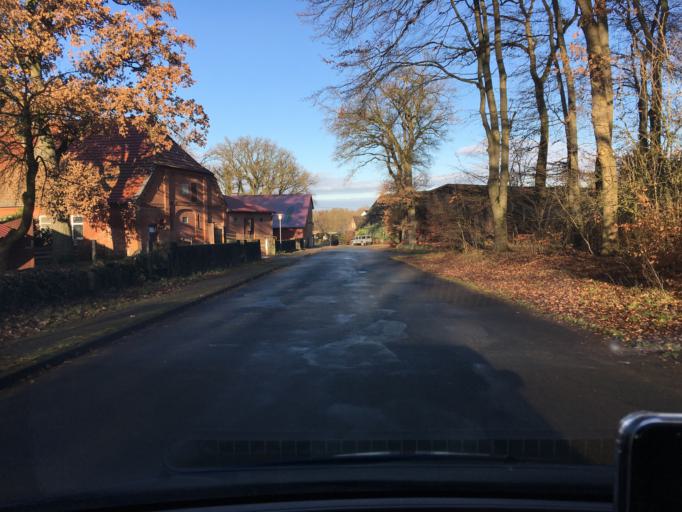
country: DE
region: Lower Saxony
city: Wendisch Evern
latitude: 53.2140
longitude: 10.4726
